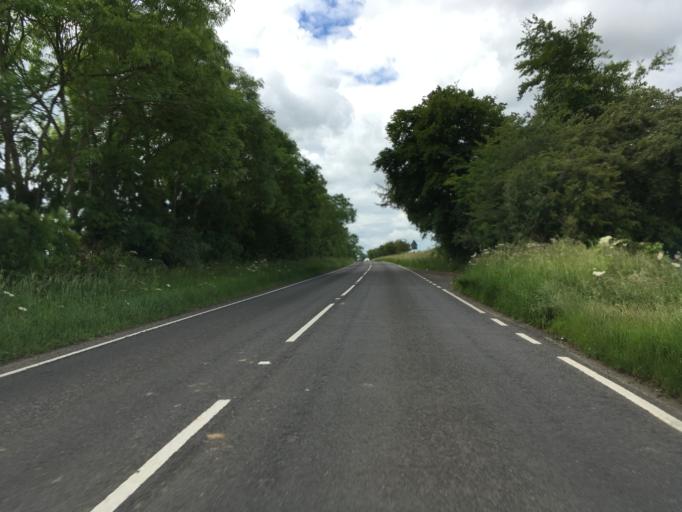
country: GB
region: England
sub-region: Oxfordshire
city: Shipton under Wychwood
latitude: 51.8772
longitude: -1.5770
